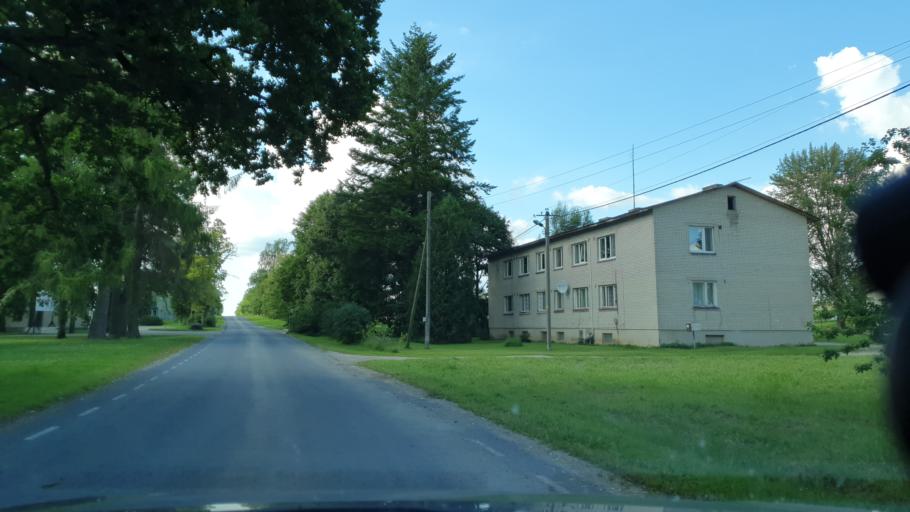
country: EE
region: Jogevamaa
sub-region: Tabivere vald
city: Tabivere
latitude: 58.6550
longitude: 26.6046
